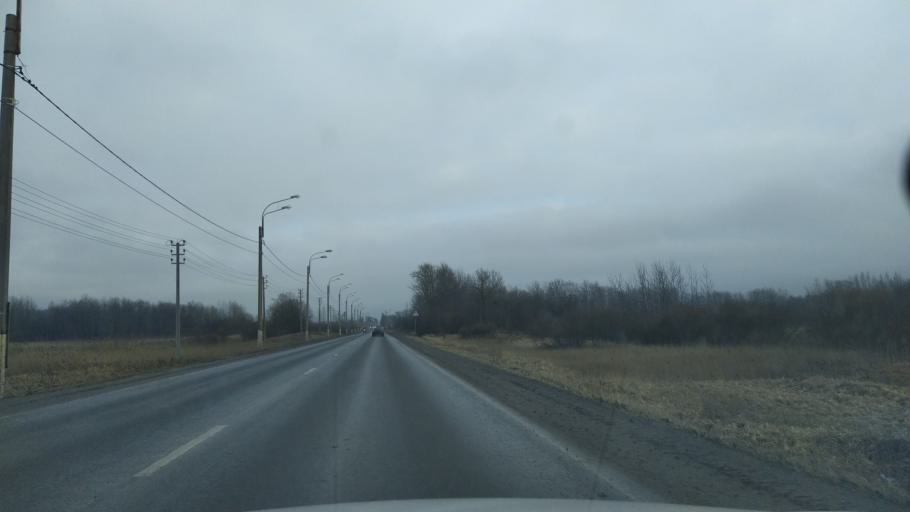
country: RU
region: St.-Petersburg
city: Aleksandrovskaya
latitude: 59.7133
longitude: 30.3051
